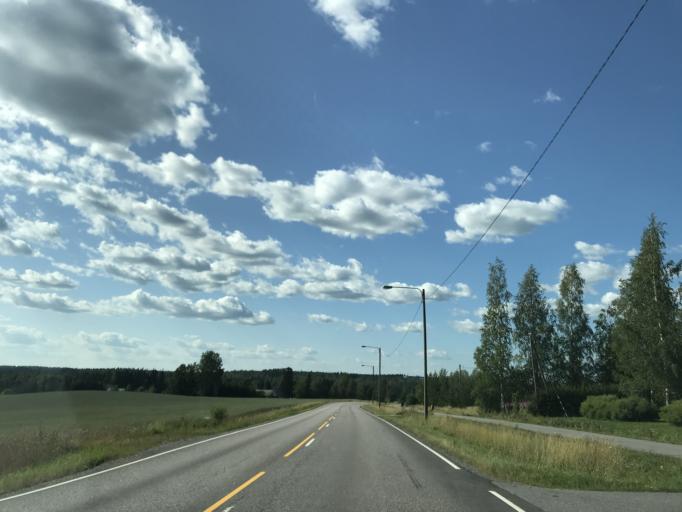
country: FI
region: Uusimaa
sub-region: Helsinki
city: Nurmijaervi
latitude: 60.4279
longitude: 24.8580
